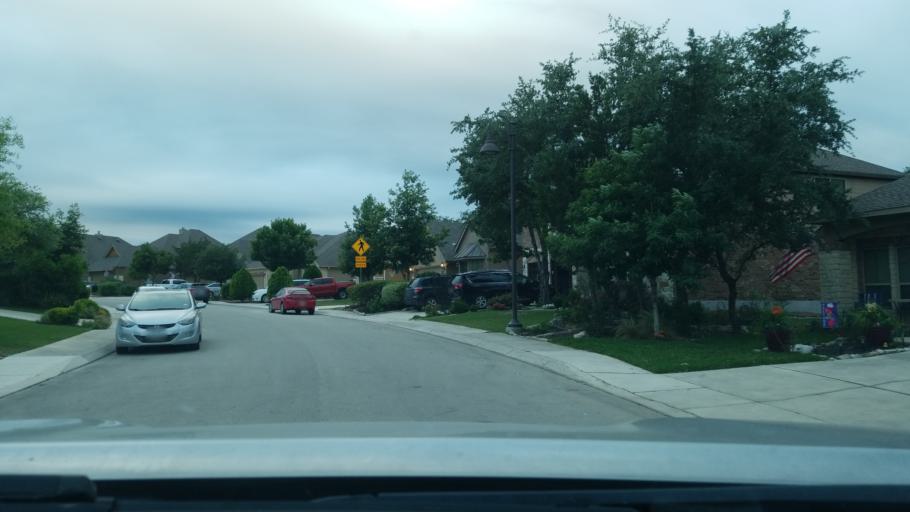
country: US
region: Texas
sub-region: Comal County
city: Bulverde
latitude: 29.7208
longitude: -98.4567
